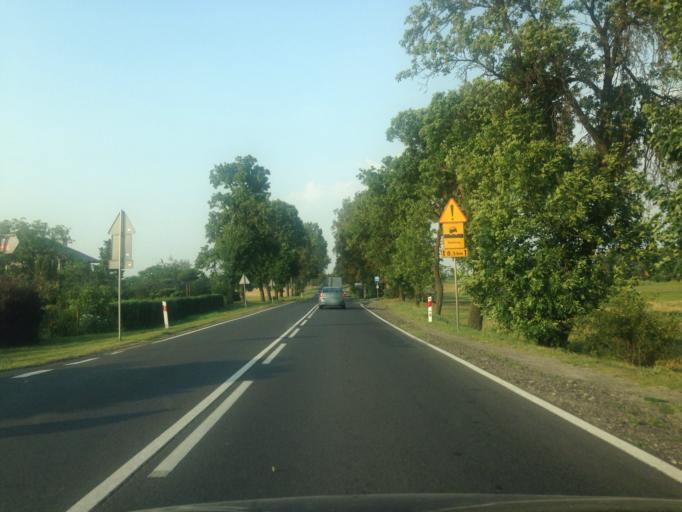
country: PL
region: Kujawsko-Pomorskie
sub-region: Powiat wloclawski
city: Fabianki
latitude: 52.7691
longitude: 19.1112
